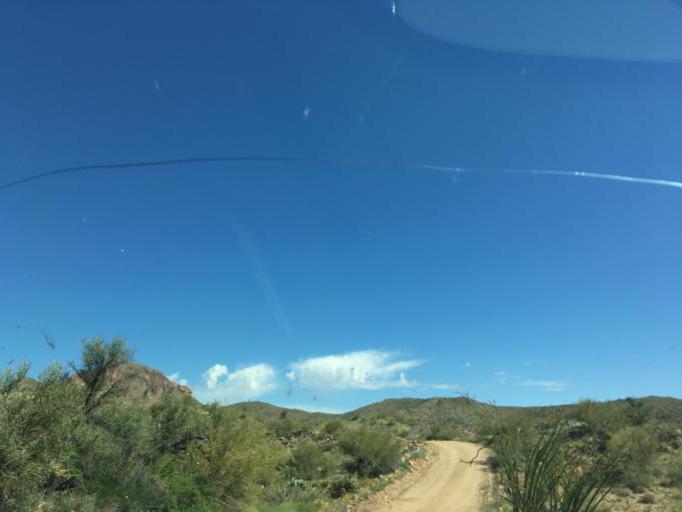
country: US
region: Arizona
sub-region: Yavapai County
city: Bagdad
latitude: 34.6037
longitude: -113.3982
